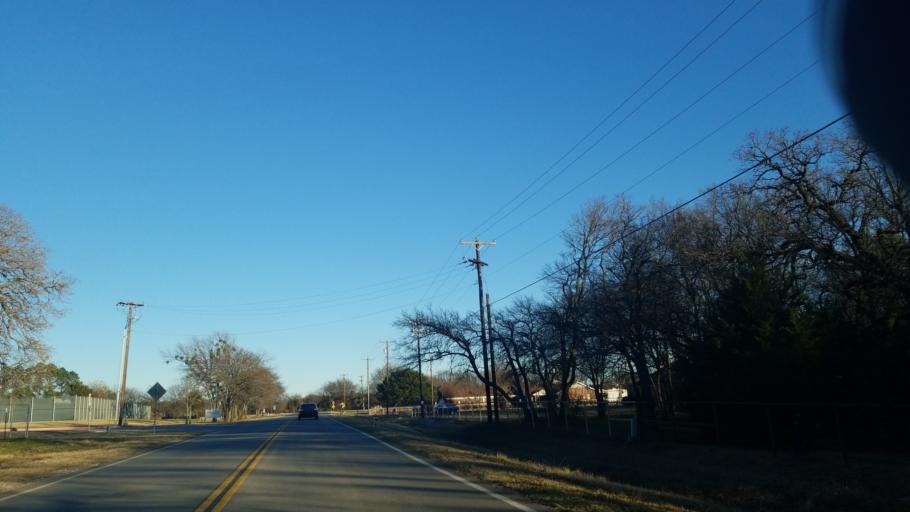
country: US
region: Texas
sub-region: Denton County
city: Shady Shores
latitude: 33.1606
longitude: -97.0430
